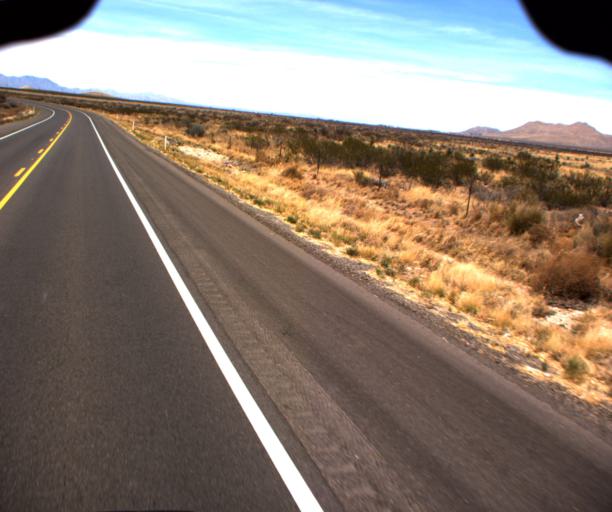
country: US
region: Arizona
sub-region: Cochise County
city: Willcox
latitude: 31.9042
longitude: -109.7170
